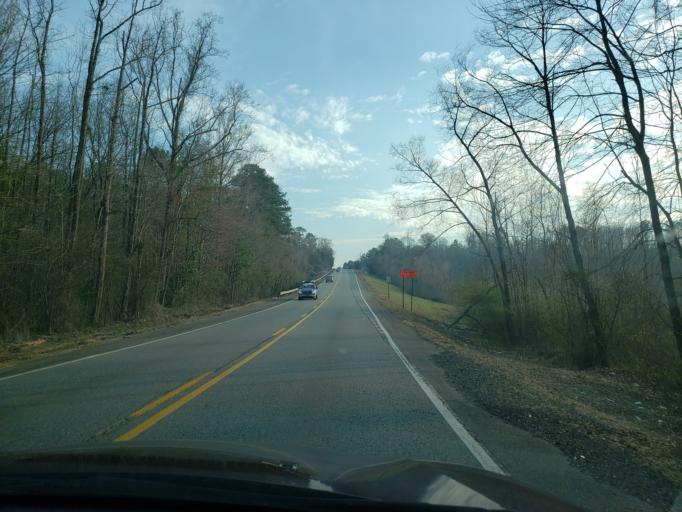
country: US
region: Alabama
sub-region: Hale County
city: Moundville
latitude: 32.9238
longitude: -87.6376
